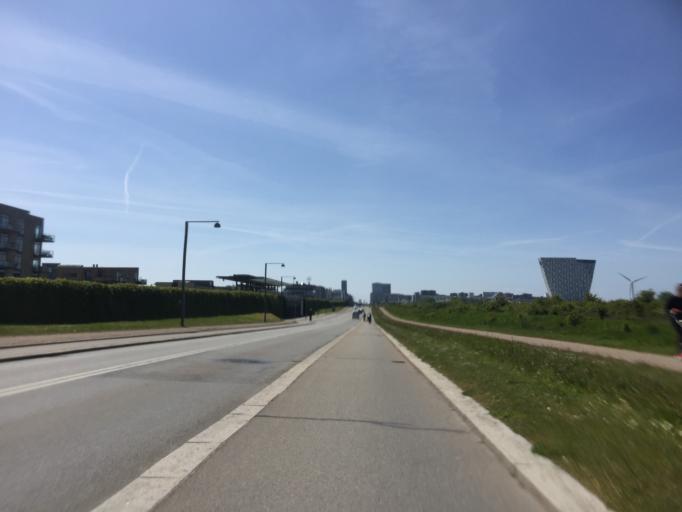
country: DK
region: Capital Region
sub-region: Tarnby Kommune
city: Tarnby
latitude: 55.6467
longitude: 12.5858
